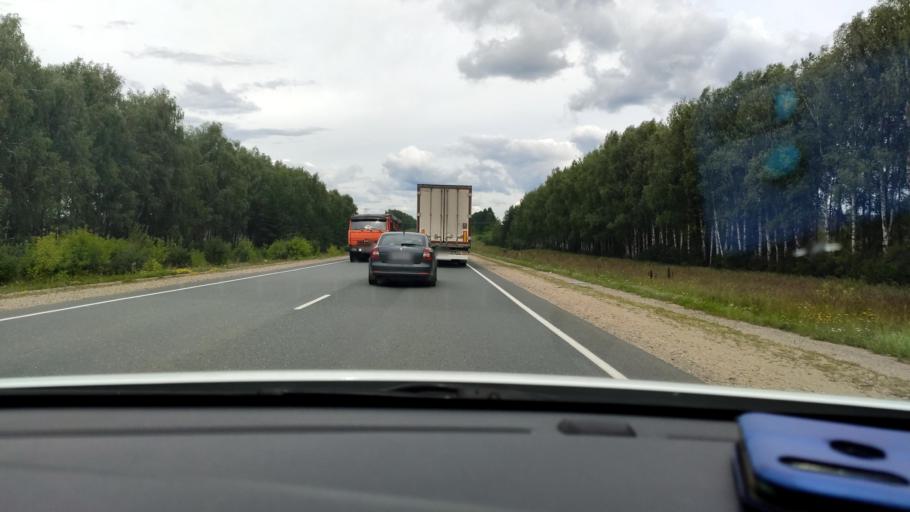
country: RU
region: Mariy-El
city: Pomary
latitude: 55.9781
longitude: 48.3739
